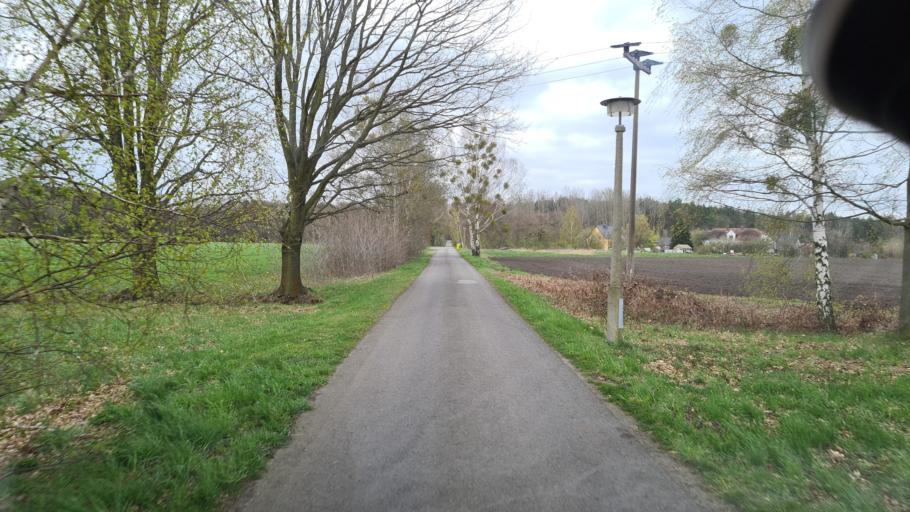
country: DE
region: Brandenburg
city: Hohenbocka
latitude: 51.4611
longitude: 14.0652
